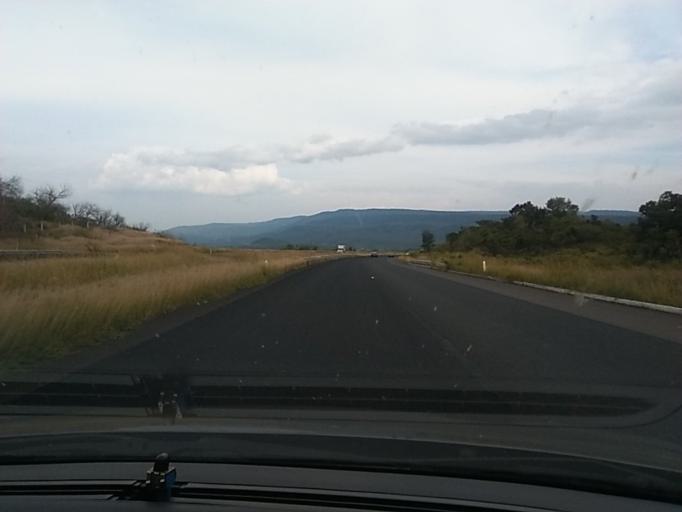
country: MX
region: Mexico
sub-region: Chapultepec
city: Chucandiro
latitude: 19.8814
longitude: -101.4115
